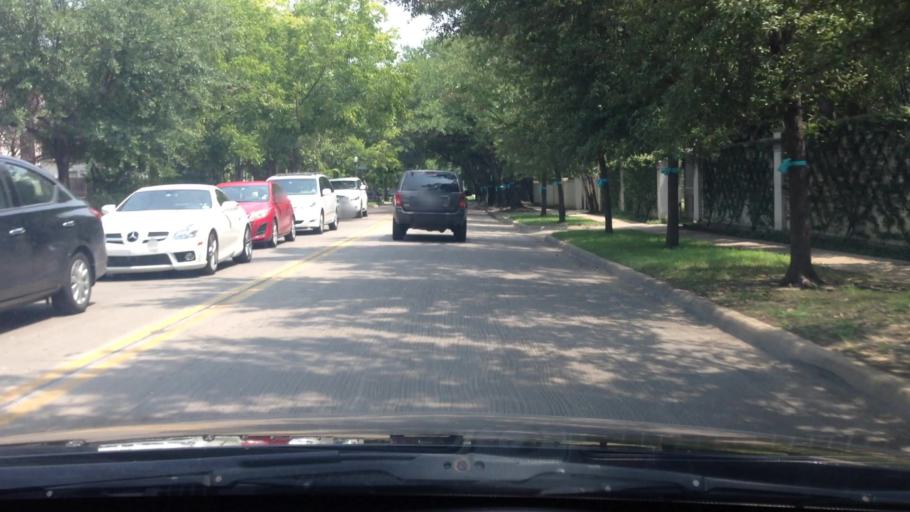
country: US
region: Texas
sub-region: Dallas County
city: University Park
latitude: 32.8510
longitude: -96.8013
